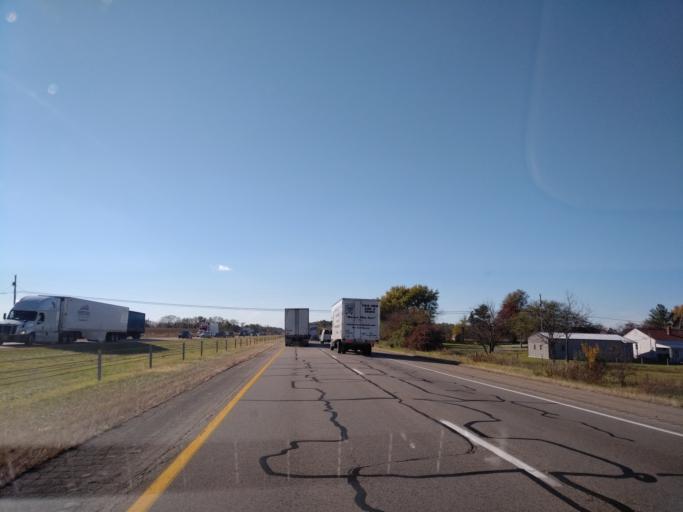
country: US
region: Indiana
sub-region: Hancock County
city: Greenfield
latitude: 39.8215
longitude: -85.7454
